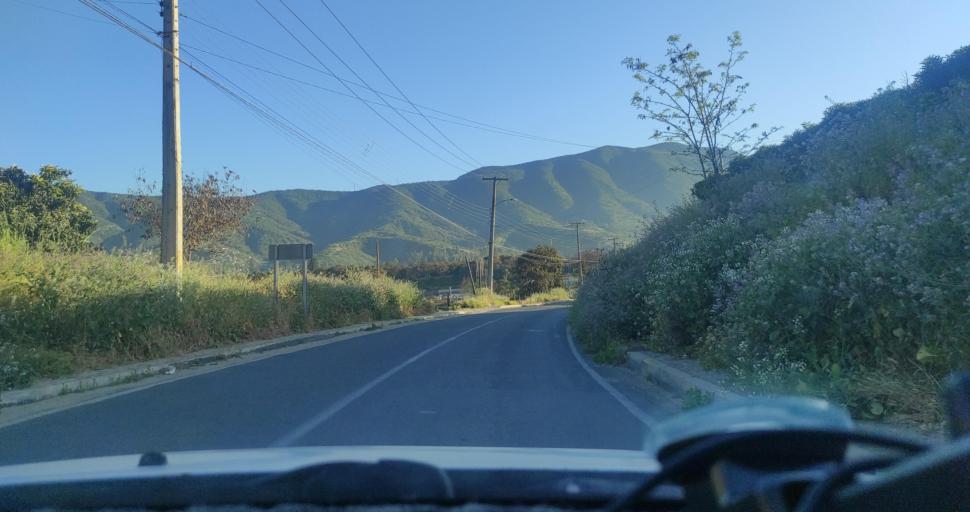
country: CL
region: Valparaiso
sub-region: Provincia de Marga Marga
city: Limache
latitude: -33.0015
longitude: -71.2239
